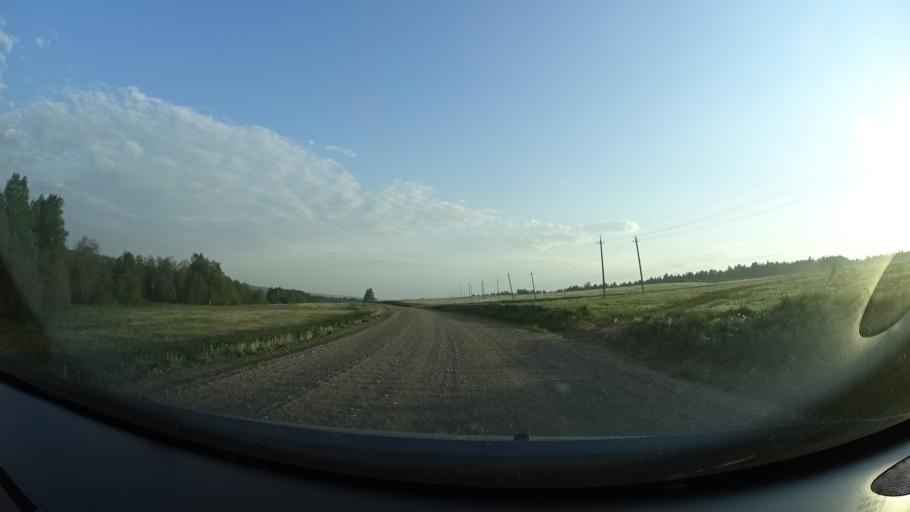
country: RU
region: Perm
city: Barda
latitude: 56.6884
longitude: 55.6867
